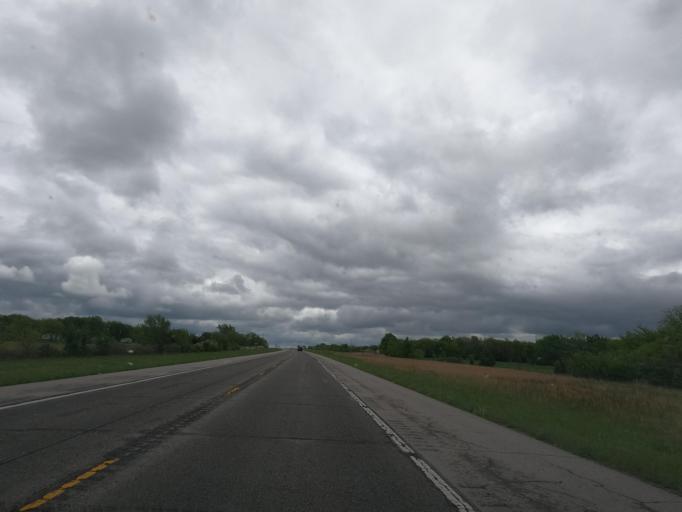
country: US
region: Kansas
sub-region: Montgomery County
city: Cherryvale
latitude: 37.3431
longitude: -95.4168
